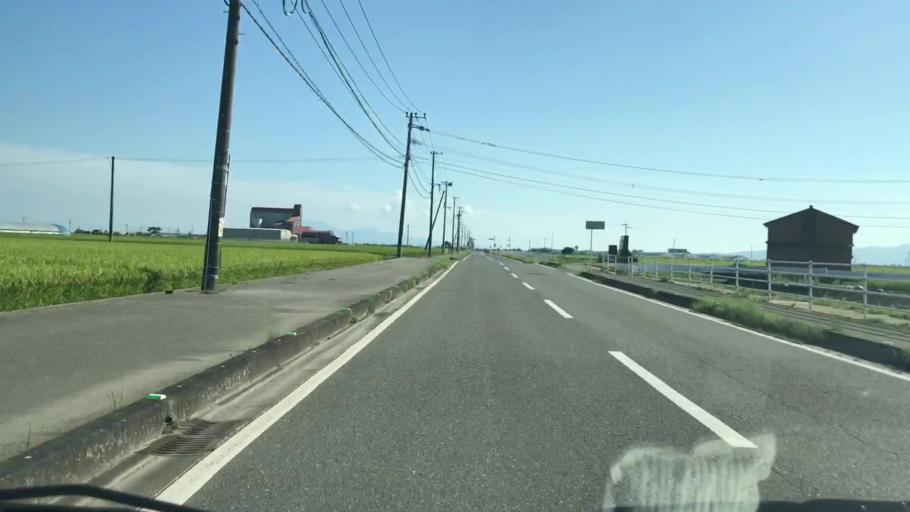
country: JP
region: Saga Prefecture
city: Okawa
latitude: 33.1784
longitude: 130.3126
